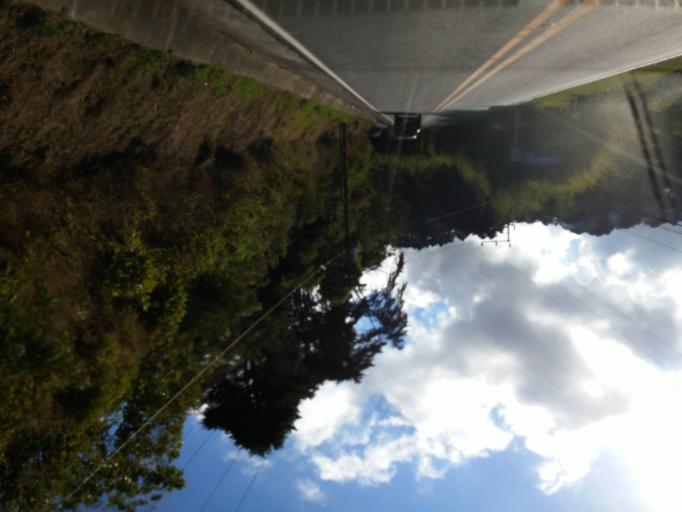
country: CR
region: San Jose
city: Salitrillos
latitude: 9.8351
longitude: -84.1007
